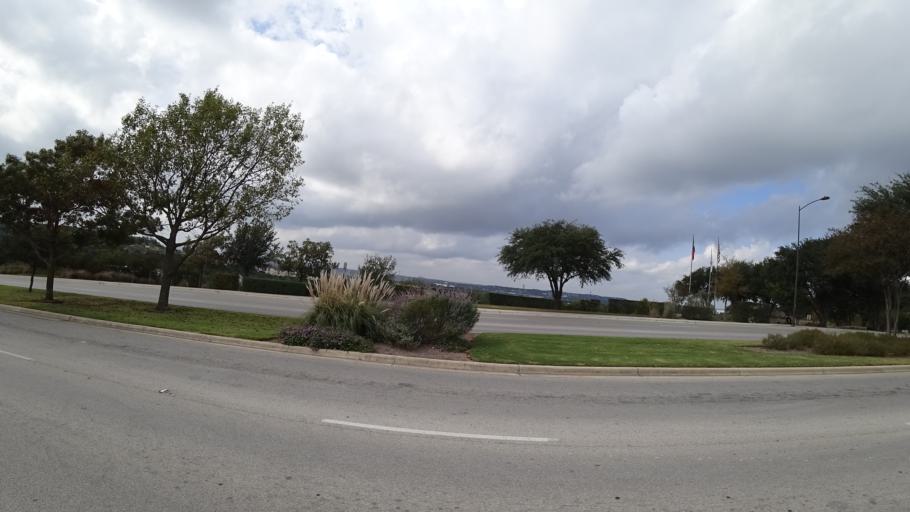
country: US
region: Texas
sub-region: Travis County
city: Hudson Bend
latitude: 30.3889
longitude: -97.8821
